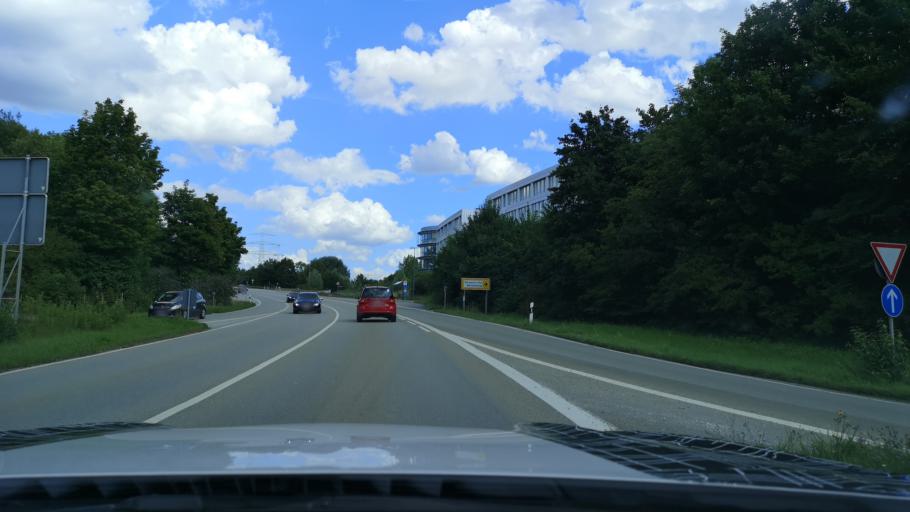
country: DE
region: Bavaria
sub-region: Upper Bavaria
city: Unterfoehring
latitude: 48.1761
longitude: 11.6387
